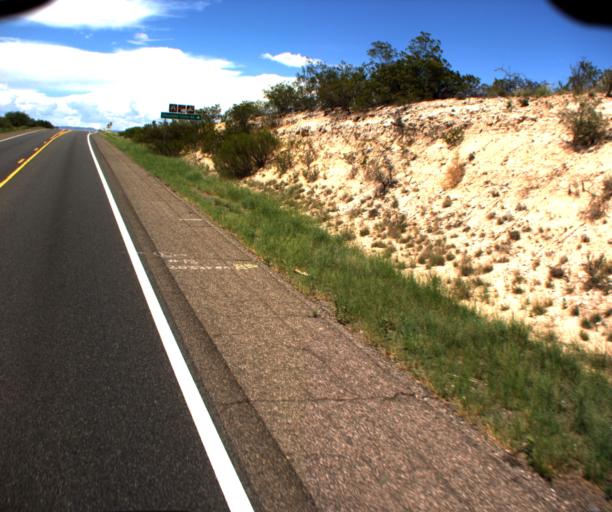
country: US
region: Arizona
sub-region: Yavapai County
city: Verde Village
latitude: 34.6592
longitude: -111.9636
